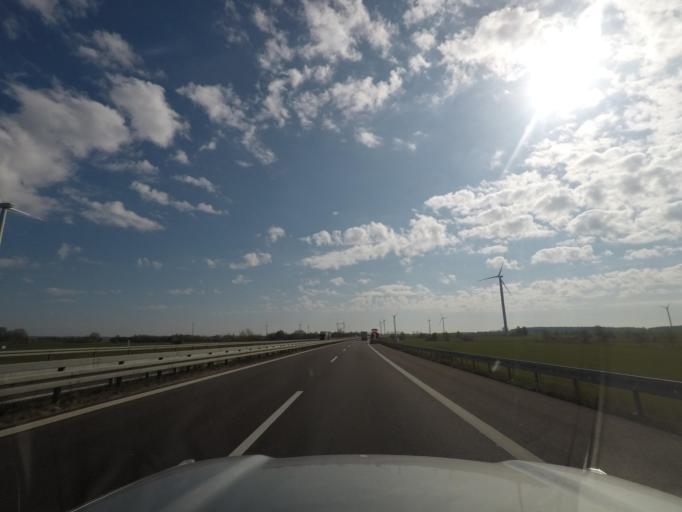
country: DE
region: Mecklenburg-Vorpommern
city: Strasburg
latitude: 53.5192
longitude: 13.8183
